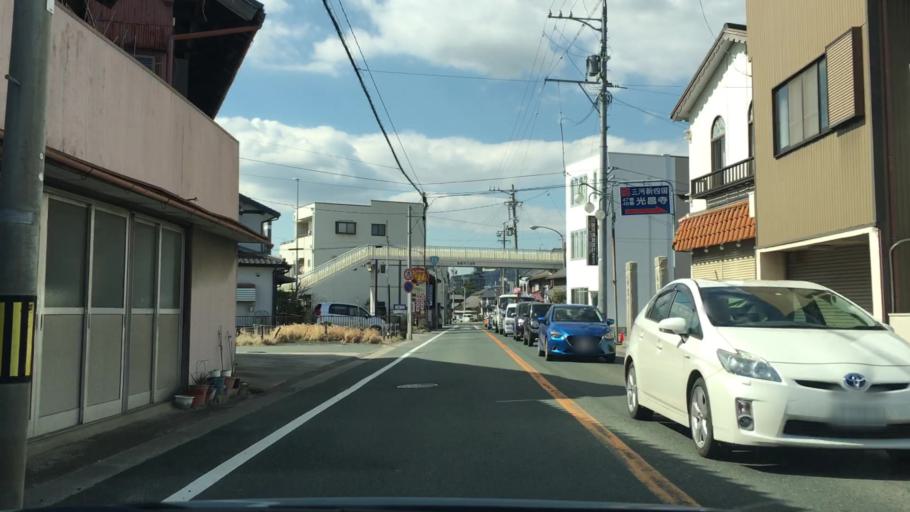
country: JP
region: Aichi
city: Gamagori
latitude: 34.8156
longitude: 137.2461
